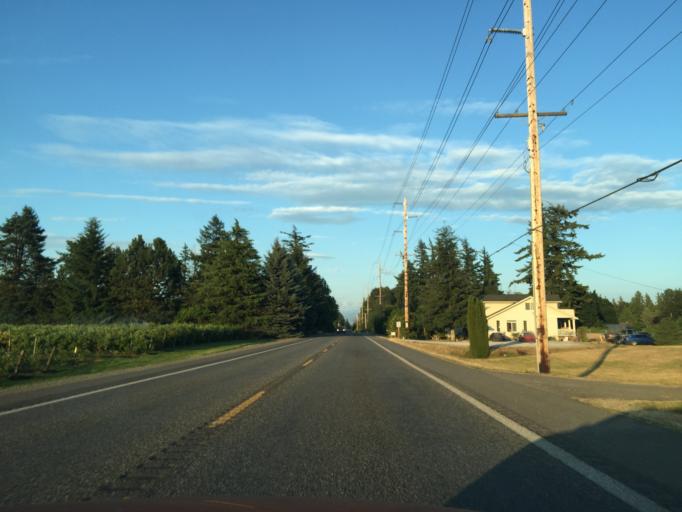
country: US
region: Washington
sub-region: Whatcom County
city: Lynden
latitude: 48.9353
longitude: -122.5441
